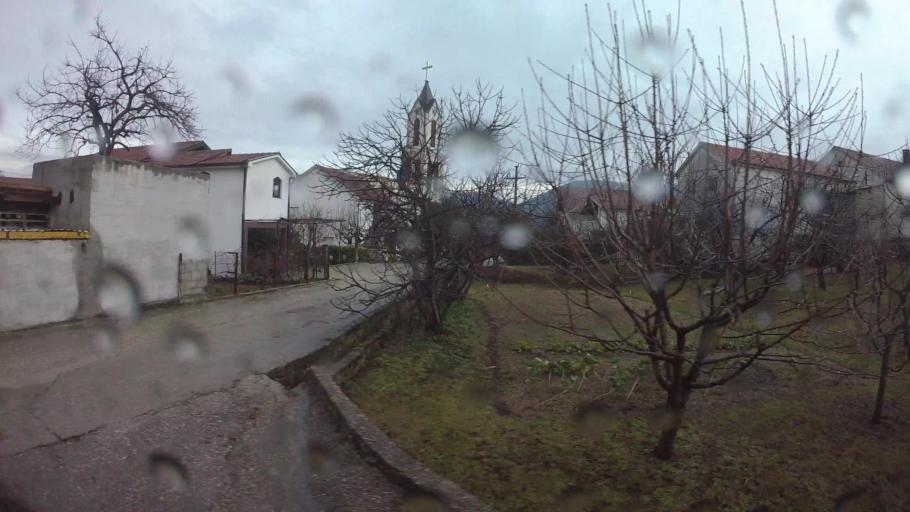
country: BA
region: Federation of Bosnia and Herzegovina
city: Cim
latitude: 43.3503
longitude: 17.7778
